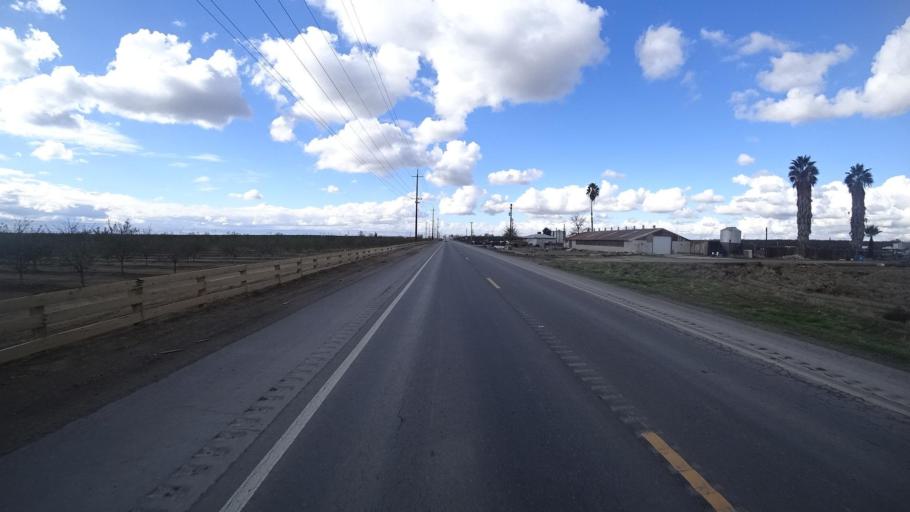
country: US
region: California
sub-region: Kern County
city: Greenfield
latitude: 35.2088
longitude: -119.0891
